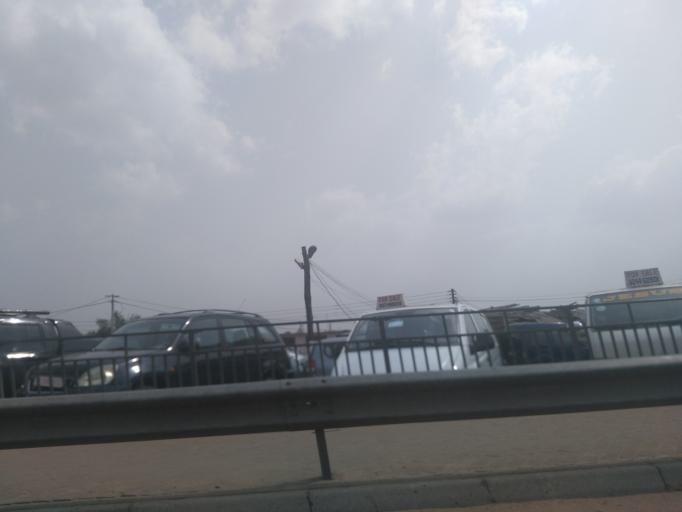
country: GH
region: Greater Accra
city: Dome
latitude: 5.6066
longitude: -0.2259
